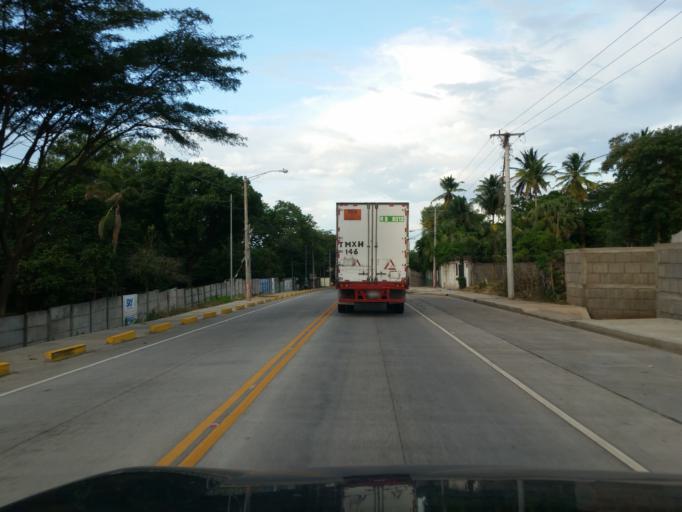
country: NI
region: Managua
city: Ciudad Sandino
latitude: 12.1038
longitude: -86.3337
